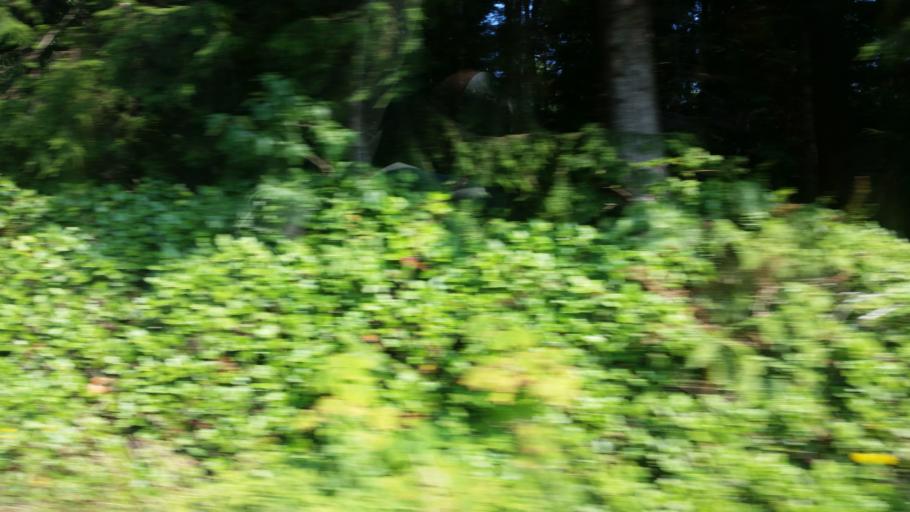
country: US
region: Washington
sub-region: Clallam County
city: Forks
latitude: 47.9128
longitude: -124.5343
